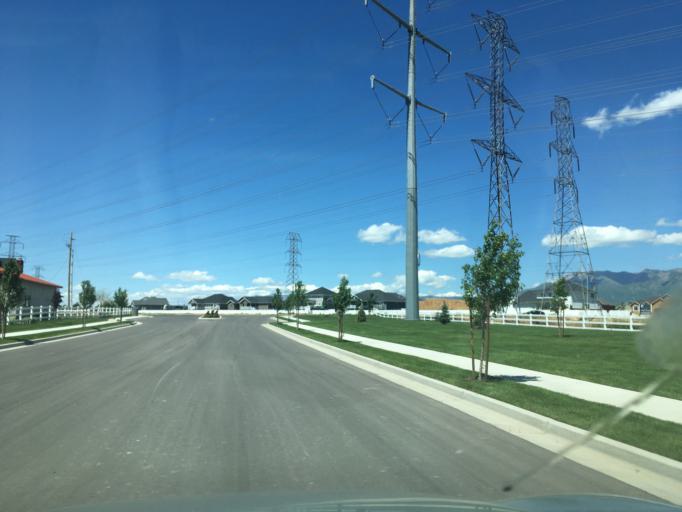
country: US
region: Utah
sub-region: Davis County
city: Layton
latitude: 41.0591
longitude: -112.0111
